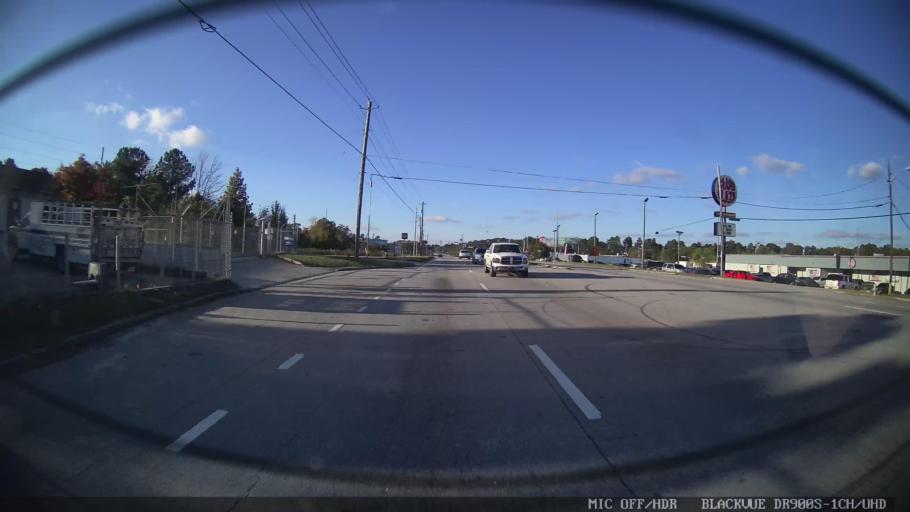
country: US
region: Georgia
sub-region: Clayton County
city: Conley
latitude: 33.6559
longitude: -84.3344
